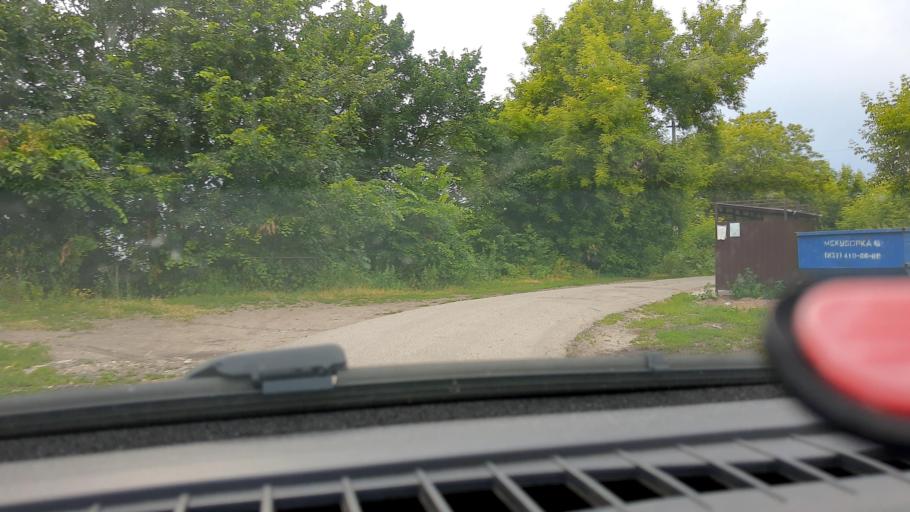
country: RU
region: Nizjnij Novgorod
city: Gorodets
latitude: 56.6331
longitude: 43.4693
